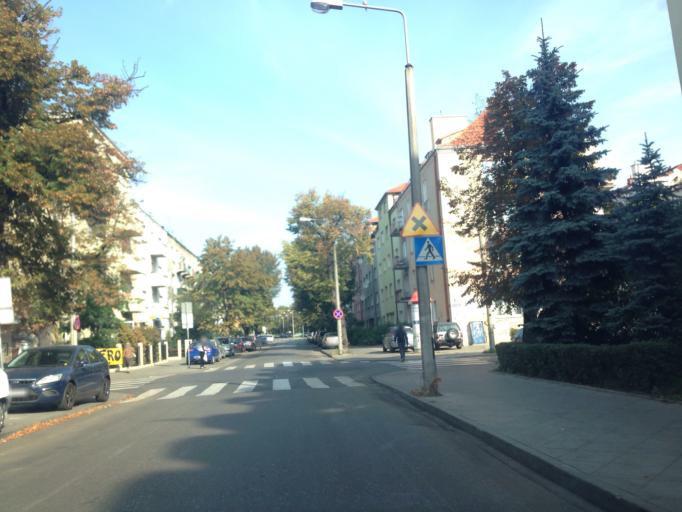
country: PL
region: Kujawsko-Pomorskie
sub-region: Torun
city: Torun
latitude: 53.0126
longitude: 18.5935
